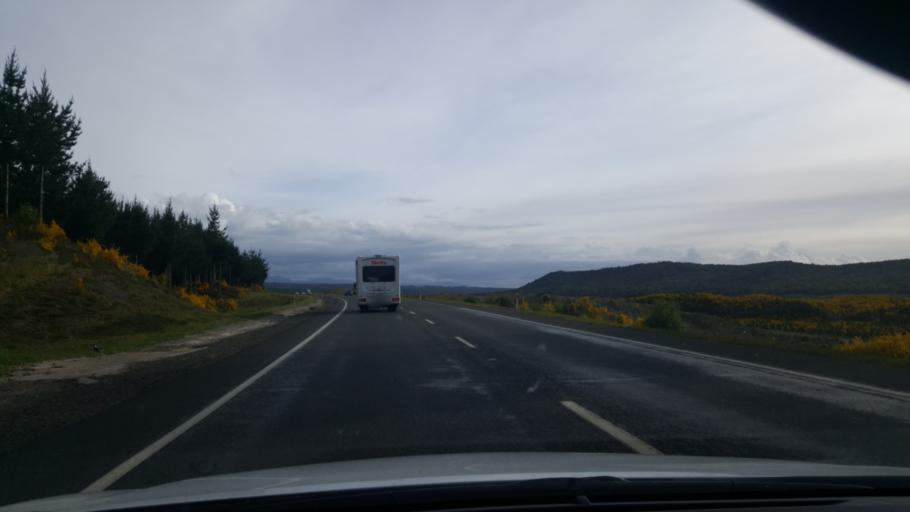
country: NZ
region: Waikato
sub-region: Taupo District
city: Taupo
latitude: -38.8289
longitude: 176.0665
